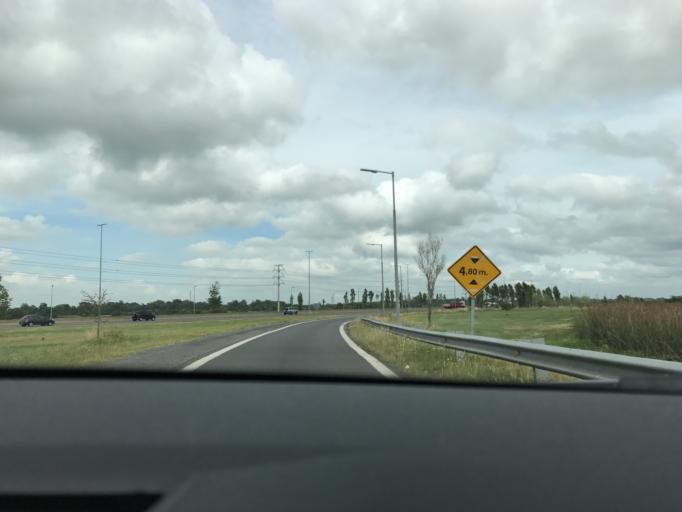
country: AR
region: Buenos Aires
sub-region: Partido de La Plata
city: La Plata
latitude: -34.8379
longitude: -58.0705
